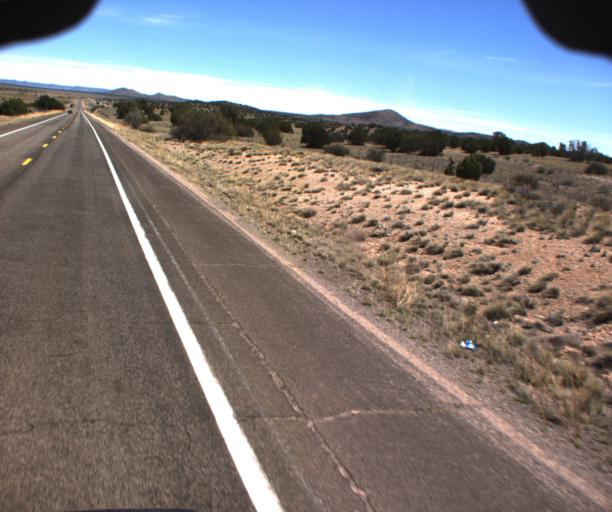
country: US
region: Arizona
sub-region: Mohave County
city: Peach Springs
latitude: 35.5522
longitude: -113.3516
